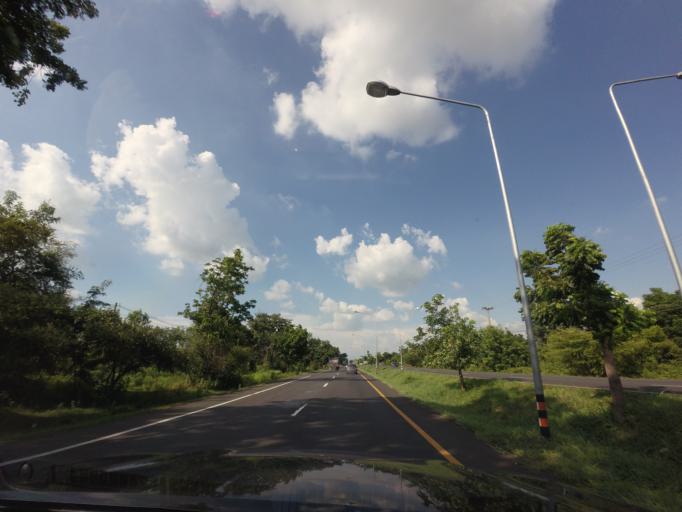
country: TH
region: Nakhon Ratchasima
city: Bua Lai
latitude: 15.7006
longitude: 102.5840
